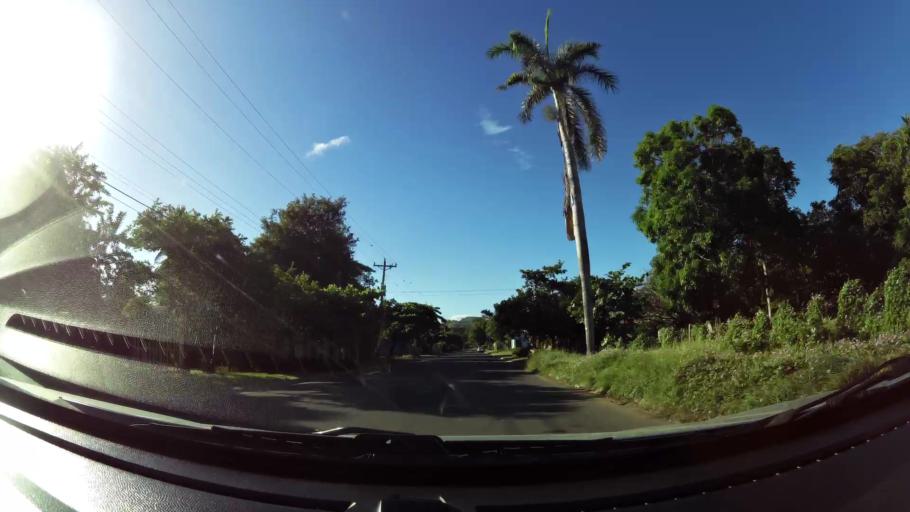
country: CR
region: Guanacaste
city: Sardinal
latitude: 10.5144
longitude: -85.6476
